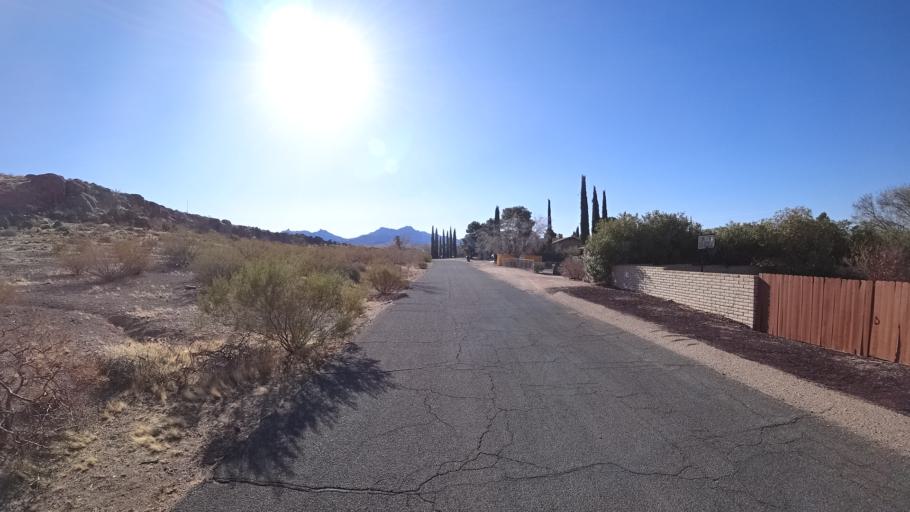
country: US
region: Arizona
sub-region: Mohave County
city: Kingman
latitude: 35.2072
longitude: -114.0069
